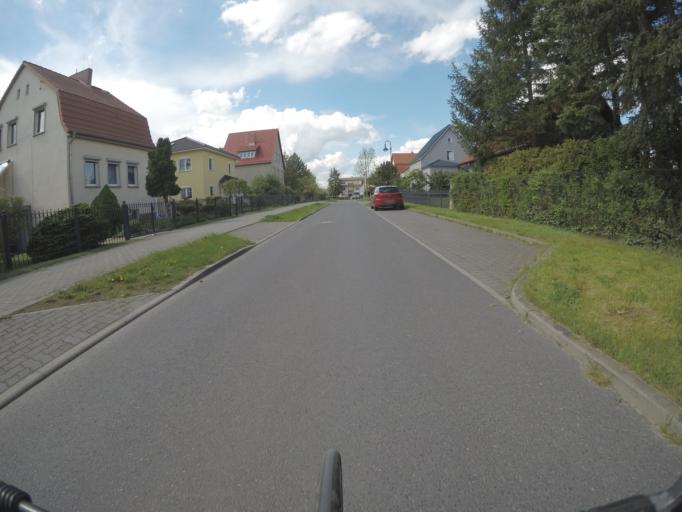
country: DE
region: Brandenburg
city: Bernau bei Berlin
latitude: 52.6638
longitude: 13.5545
